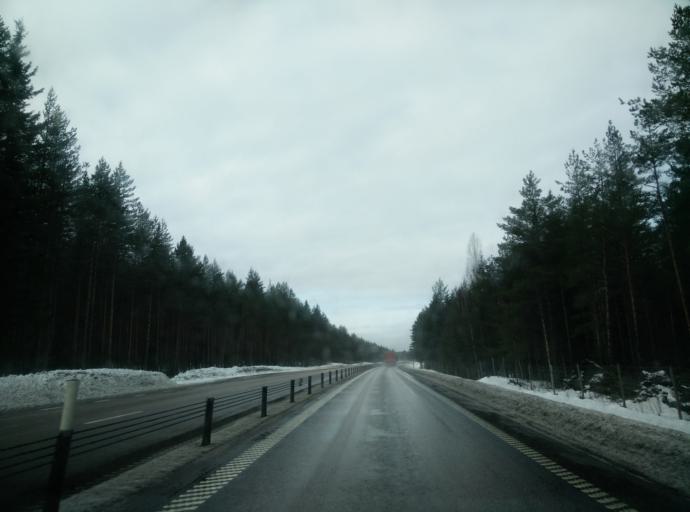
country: SE
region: Dalarna
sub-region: Hedemora Kommun
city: Langshyttan
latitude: 60.5548
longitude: 16.0812
